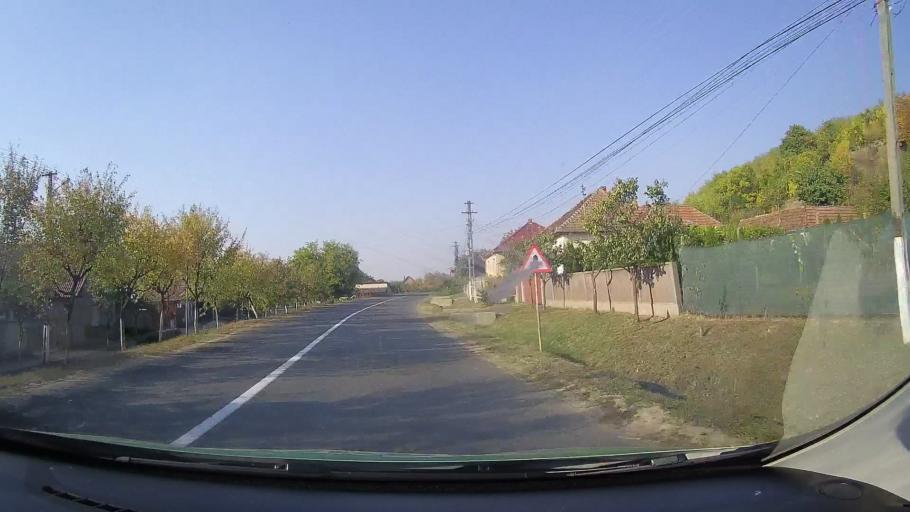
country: RO
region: Arad
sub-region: Comuna Paulis
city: Paulis
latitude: 46.1146
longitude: 21.5963
